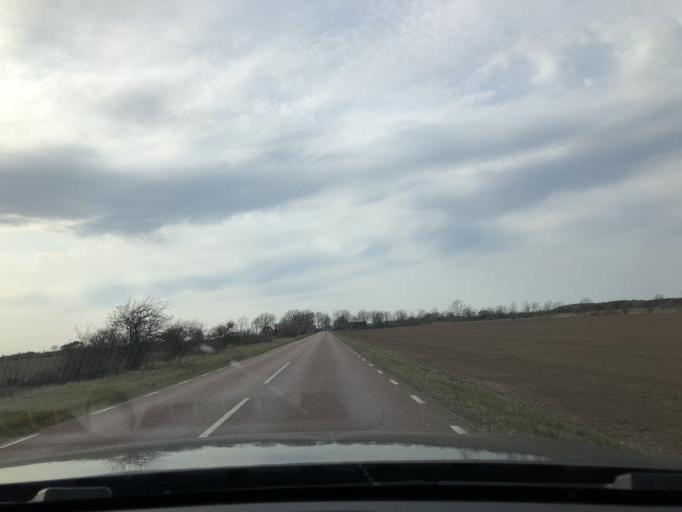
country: SE
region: Kalmar
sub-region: Morbylanga Kommun
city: Moerbylanga
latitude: 56.2873
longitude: 16.4871
